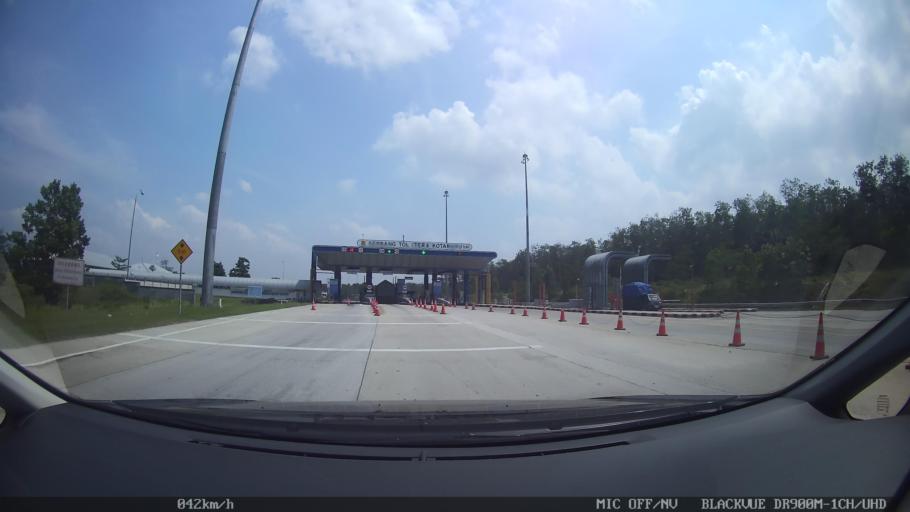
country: ID
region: Lampung
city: Kedaton
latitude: -5.3590
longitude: 105.3274
